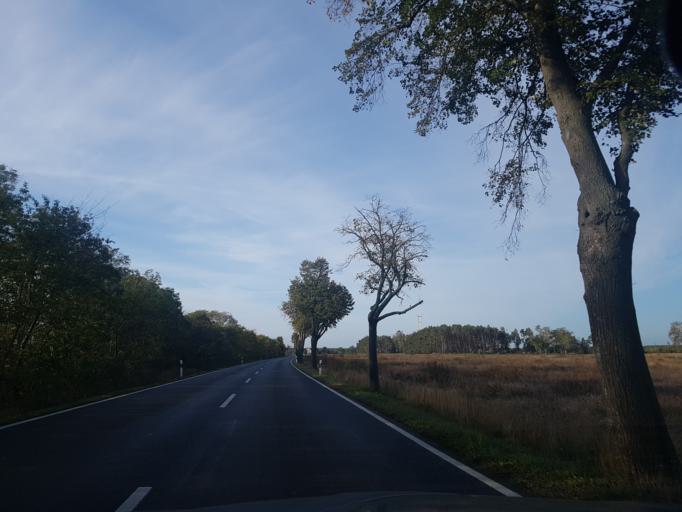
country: DE
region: Saxony
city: Arzberg
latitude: 51.6048
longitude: 13.1333
